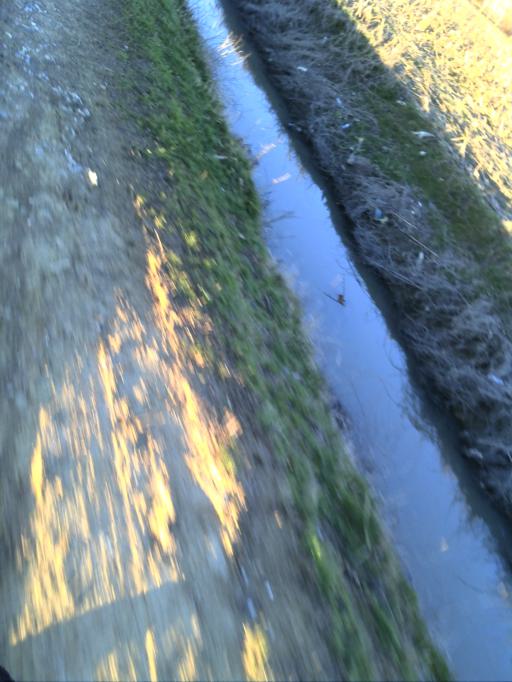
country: AL
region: Shkoder
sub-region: Rrethi i Shkodres
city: Berdica e Madhe
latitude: 41.9660
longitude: 19.4737
